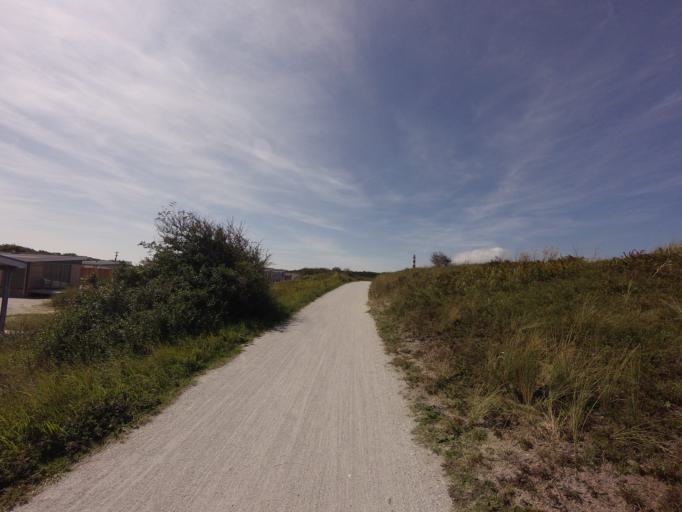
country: NL
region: Friesland
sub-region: Gemeente Ameland
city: Hollum
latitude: 53.4512
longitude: 5.6342
